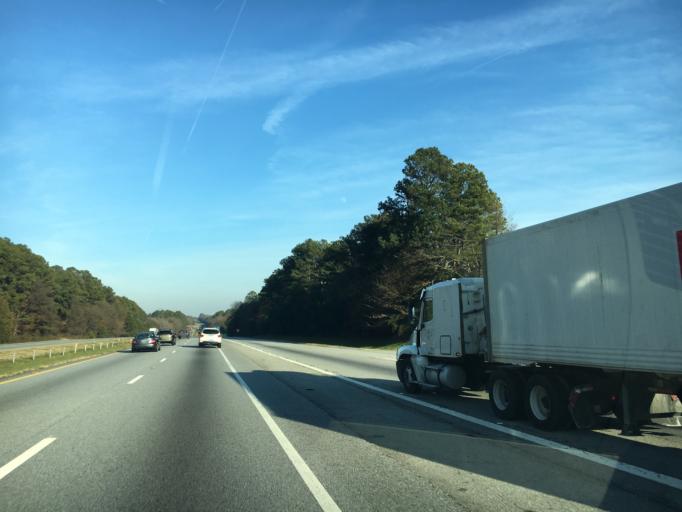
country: US
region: Georgia
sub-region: Hart County
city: Reed Creek
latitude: 34.5172
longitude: -82.8725
